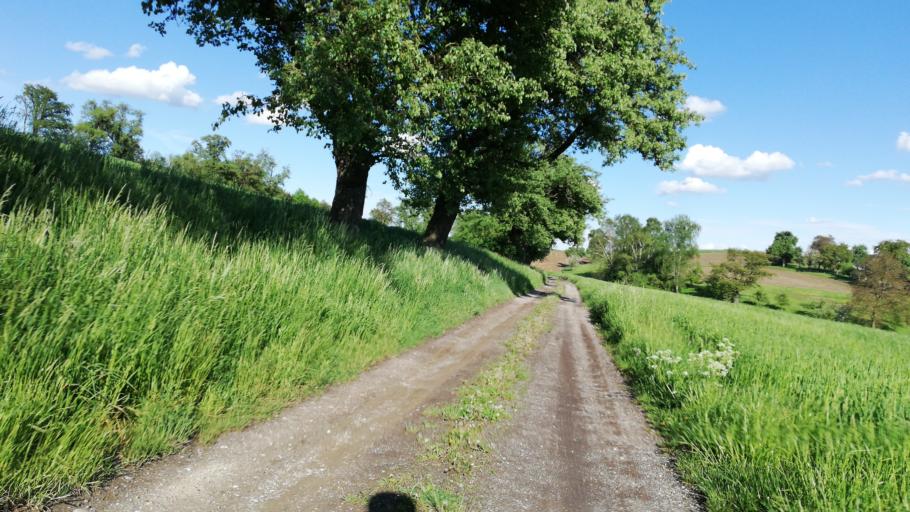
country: AT
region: Upper Austria
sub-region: Politischer Bezirk Grieskirchen
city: Bad Schallerbach
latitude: 48.2078
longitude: 13.9385
